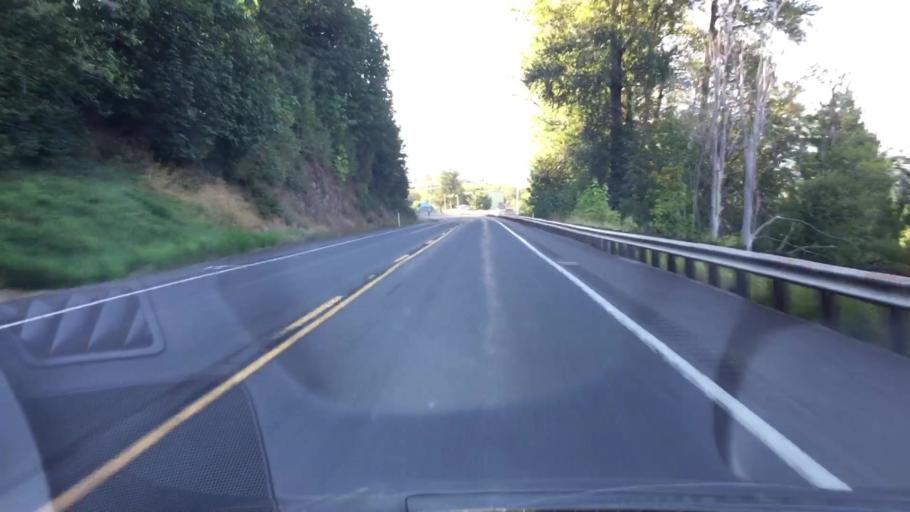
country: US
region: Washington
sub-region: Lewis County
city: Morton
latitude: 46.5295
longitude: -122.2388
